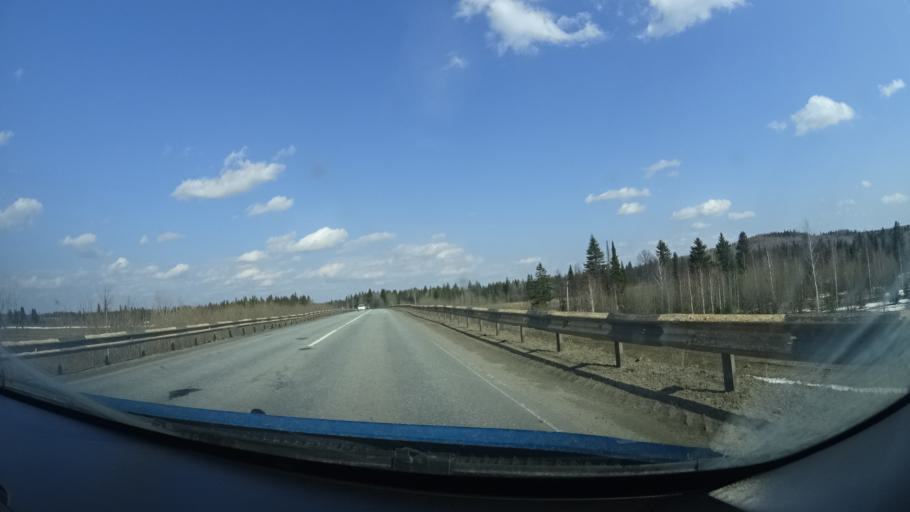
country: RU
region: Perm
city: Yugo-Kamskiy
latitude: 57.7824
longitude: 55.7670
